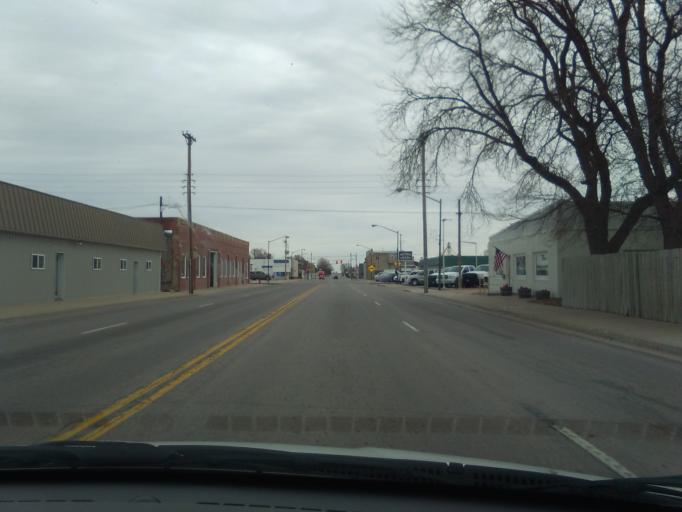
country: US
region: Colorado
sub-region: Washington County
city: Akron
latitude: 40.1591
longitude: -103.2104
